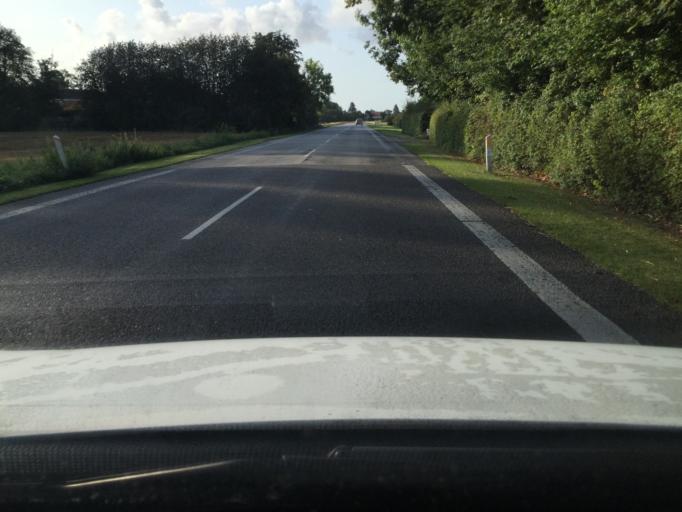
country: DK
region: Zealand
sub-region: Lolland Kommune
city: Rodby
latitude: 54.7802
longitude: 11.2959
